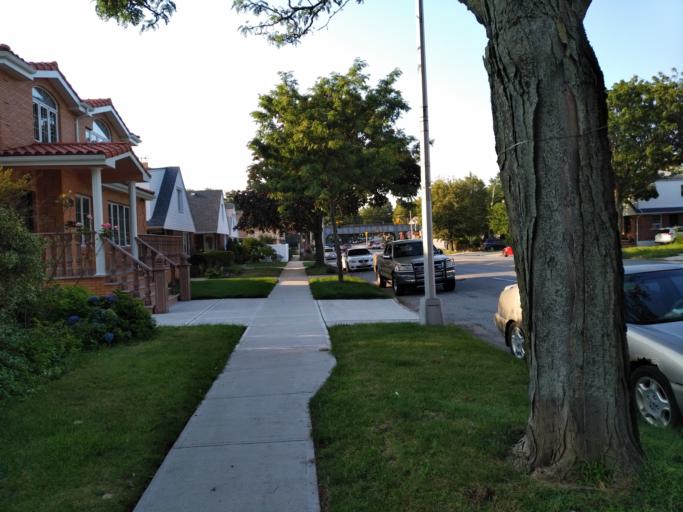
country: US
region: New York
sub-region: Nassau County
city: East Atlantic Beach
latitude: 40.7599
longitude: -73.7935
